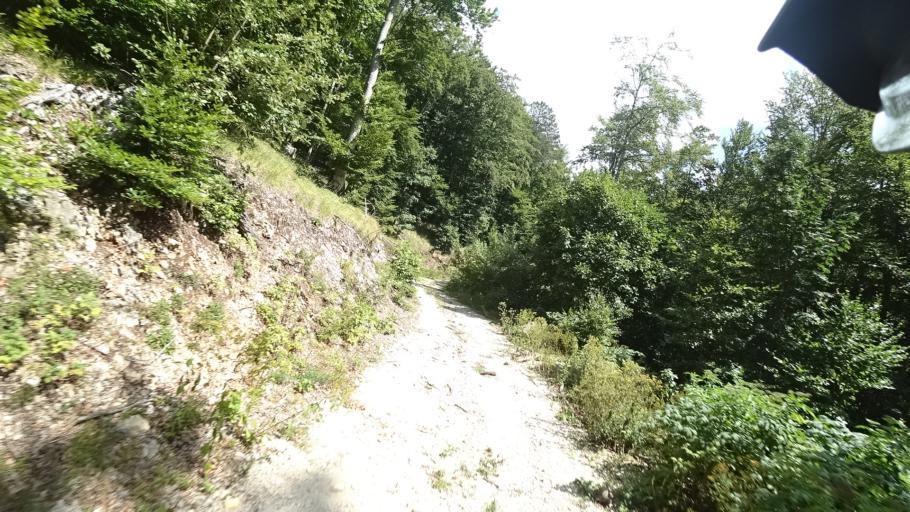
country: BA
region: Federation of Bosnia and Herzegovina
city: Orasac
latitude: 44.5644
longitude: 15.8545
